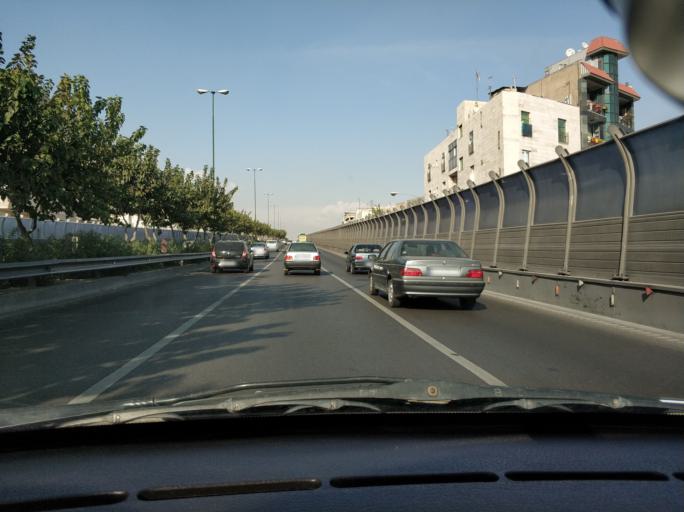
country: IR
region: Tehran
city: Tehran
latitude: 35.7176
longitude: 51.3569
